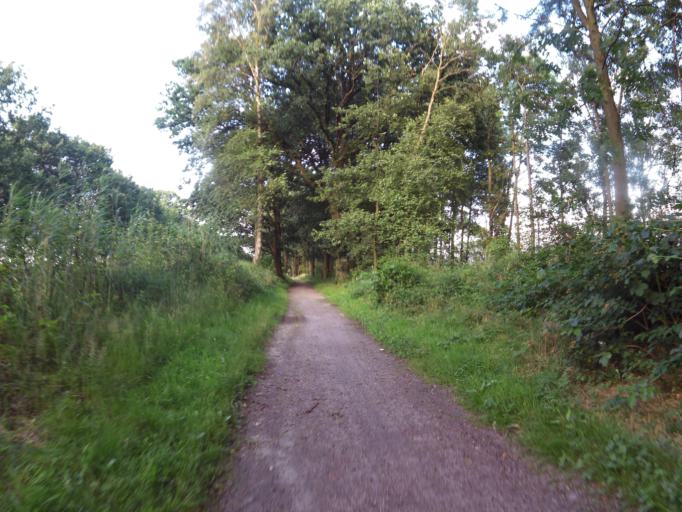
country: NL
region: North Brabant
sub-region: Gemeente Geldrop-Mierlo
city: Geldrop
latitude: 51.4376
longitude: 5.5566
